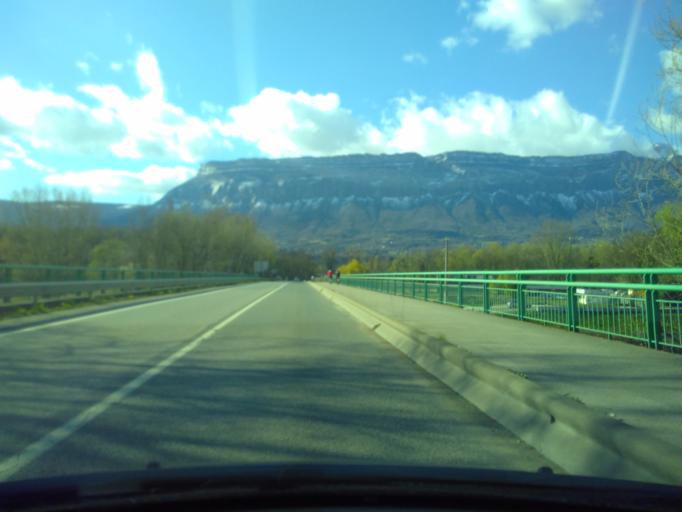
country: FR
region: Rhone-Alpes
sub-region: Departement de l'Isere
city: Domene
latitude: 45.2116
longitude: 5.8304
